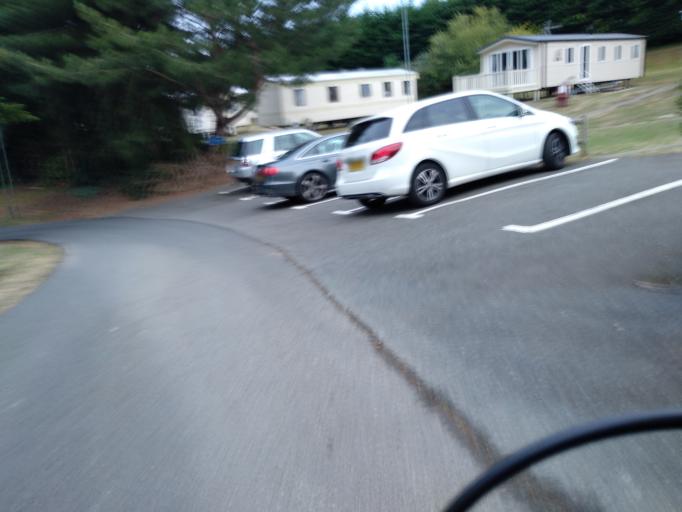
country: GB
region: England
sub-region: Isle of Wight
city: Shanklin
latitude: 50.6358
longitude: -1.1860
